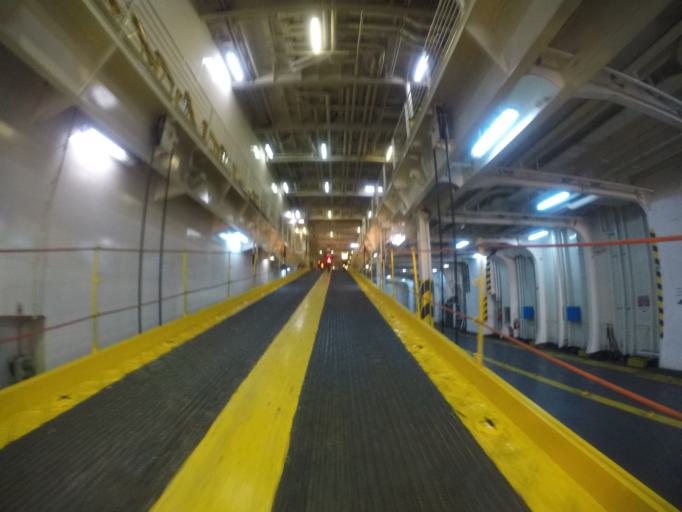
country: IT
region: Sardinia
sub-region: Provincia di Cagliari
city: Cagliari
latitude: 39.2119
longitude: 9.1057
